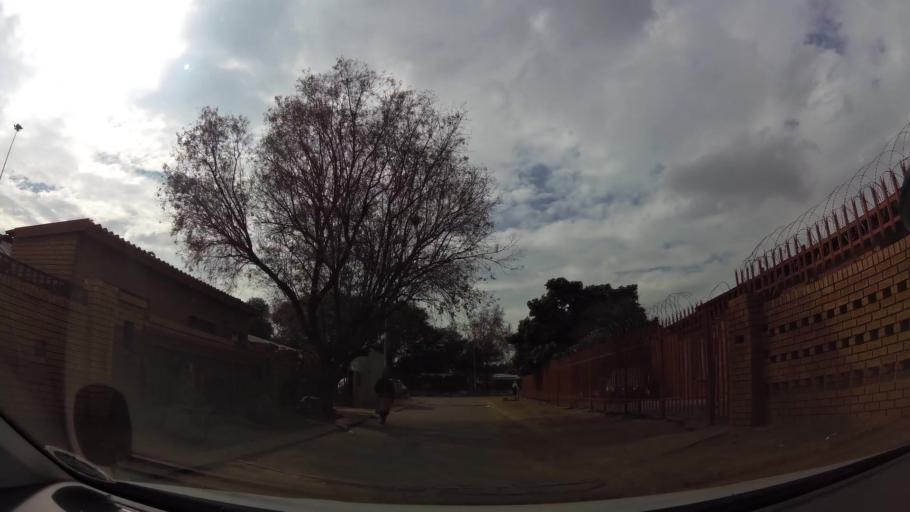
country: ZA
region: Gauteng
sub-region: City of Johannesburg Metropolitan Municipality
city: Soweto
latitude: -26.2711
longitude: 27.8552
